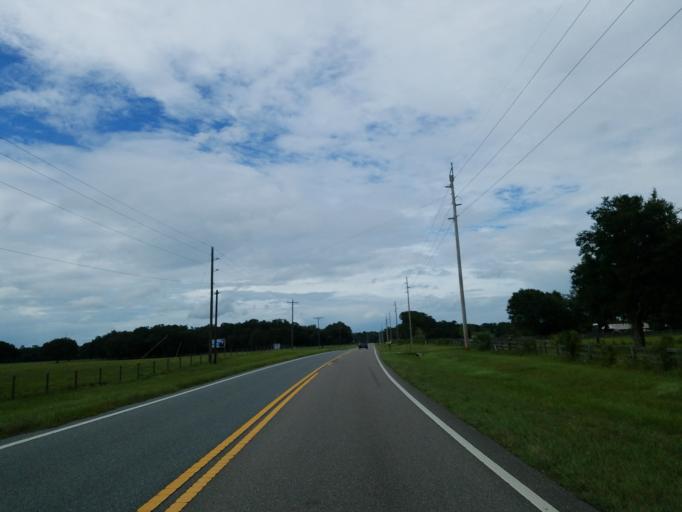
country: US
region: Florida
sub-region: Sumter County
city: Lake Panasoffkee
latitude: 28.8338
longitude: -82.1777
